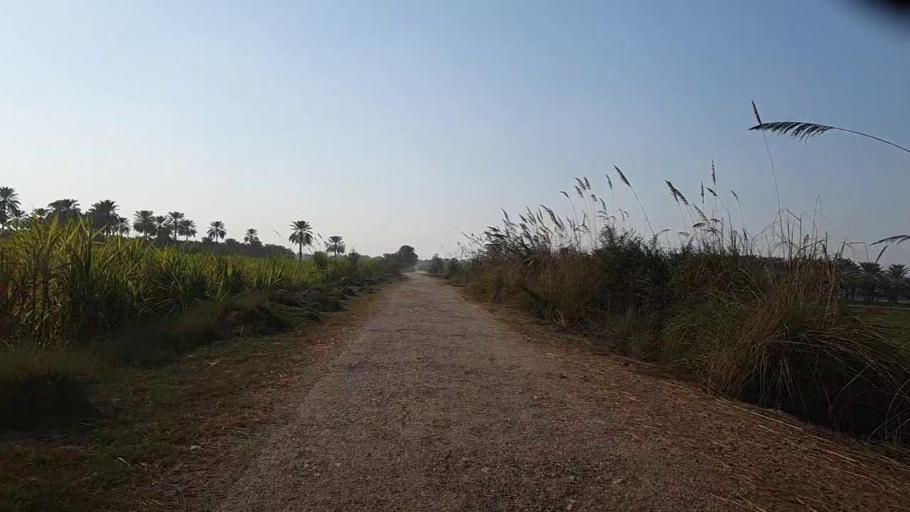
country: PK
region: Sindh
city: Ranipur
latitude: 27.2513
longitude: 68.5537
